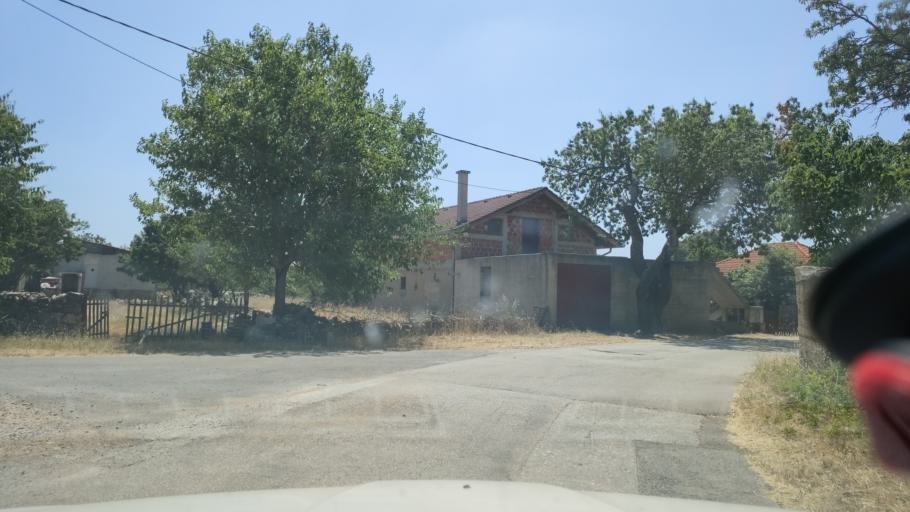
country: HR
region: Sibensko-Kniniska
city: Kistanje
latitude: 43.9504
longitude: 15.8831
